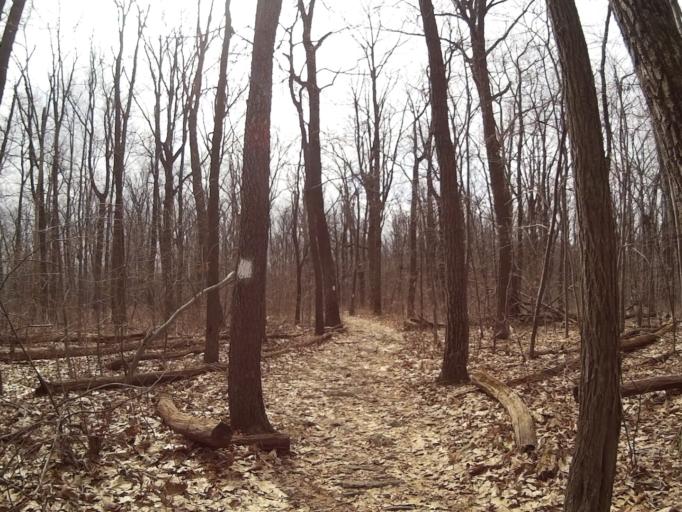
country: US
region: Pennsylvania
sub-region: Centre County
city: Lemont
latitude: 40.8098
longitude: -77.7993
